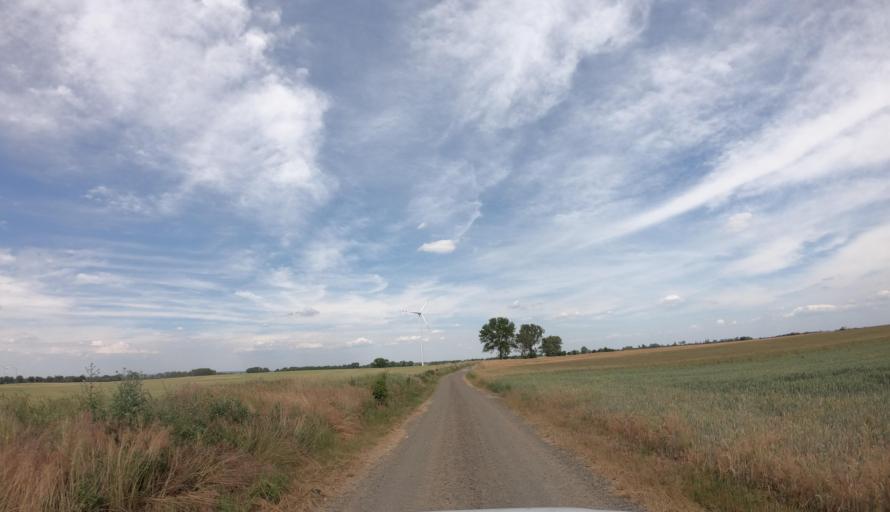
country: PL
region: West Pomeranian Voivodeship
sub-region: Powiat pyrzycki
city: Kozielice
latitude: 53.1161
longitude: 14.8275
